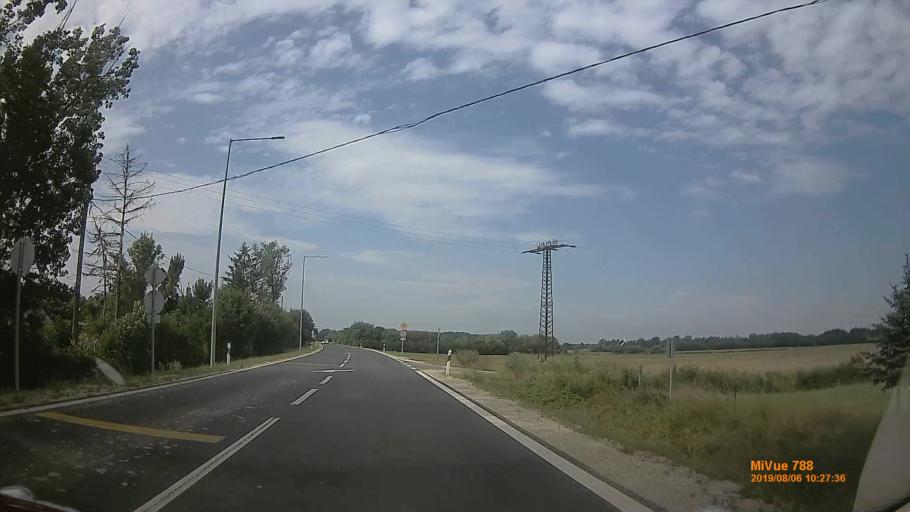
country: HU
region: Vas
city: Kormend
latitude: 47.0424
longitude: 16.6670
